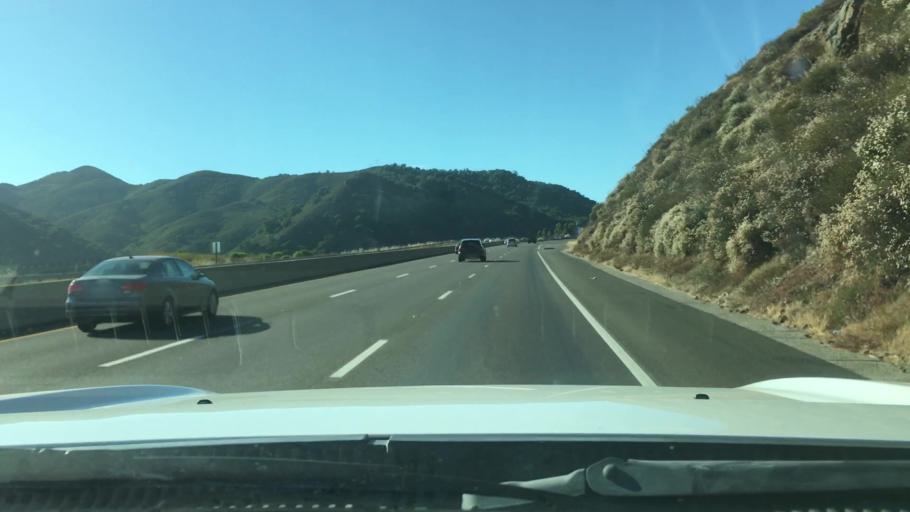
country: US
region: California
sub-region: San Luis Obispo County
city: Santa Margarita
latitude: 35.3358
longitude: -120.6256
